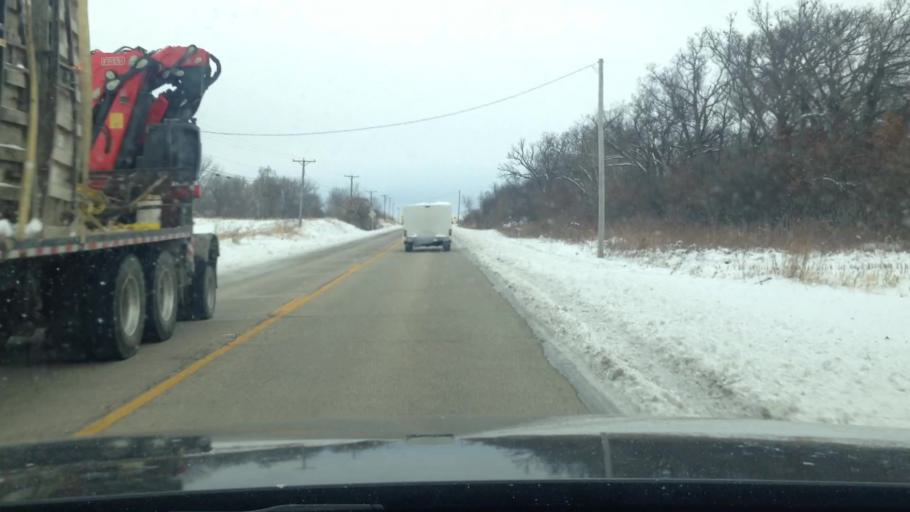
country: US
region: Illinois
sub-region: McHenry County
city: Hebron
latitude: 42.4892
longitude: -88.4424
